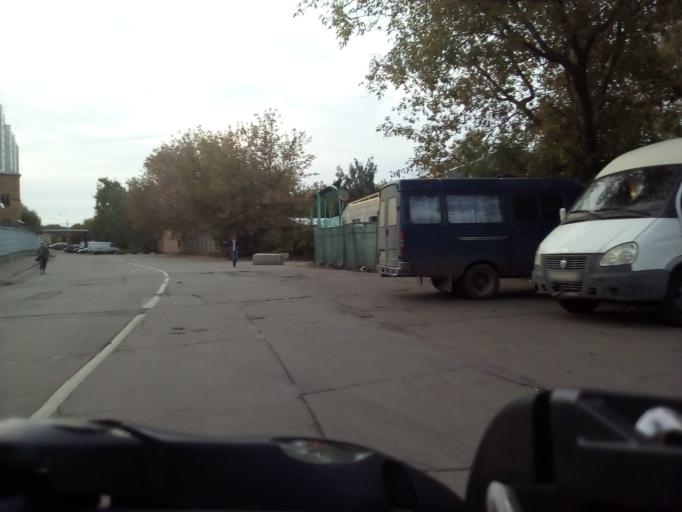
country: RU
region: Moscow
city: Leonovo
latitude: 55.8378
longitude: 37.6485
